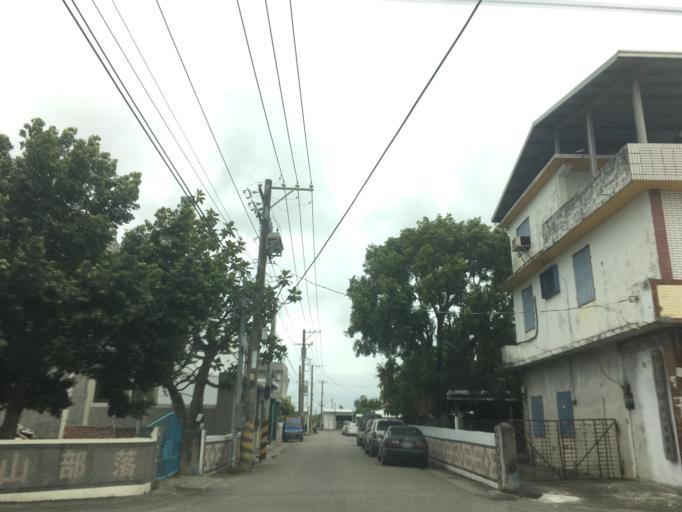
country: TW
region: Taiwan
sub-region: Taitung
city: Taitung
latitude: 22.7837
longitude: 121.1605
